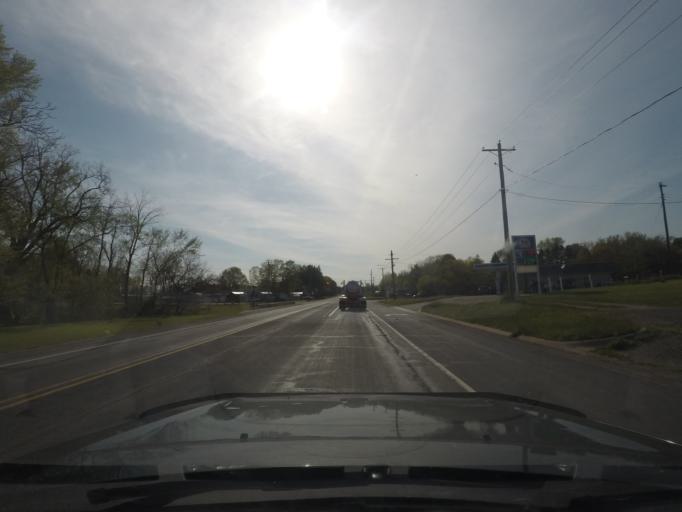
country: US
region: Indiana
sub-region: LaPorte County
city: Hudson Lake
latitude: 41.7980
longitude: -86.4978
